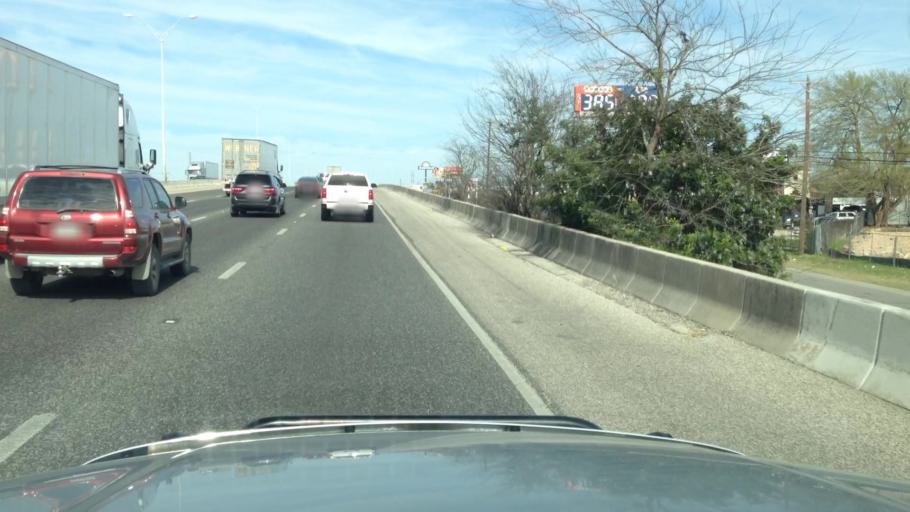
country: US
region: Texas
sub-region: Bexar County
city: Windcrest
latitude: 29.5380
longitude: -98.3805
